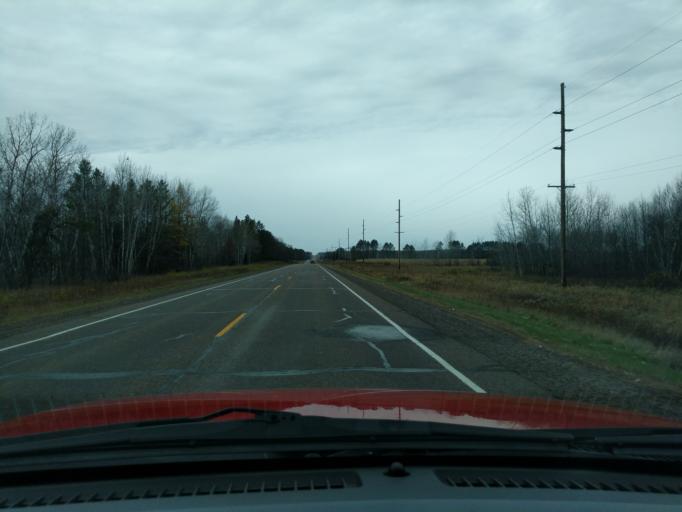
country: US
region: Wisconsin
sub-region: Washburn County
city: Shell Lake
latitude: 45.8151
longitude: -91.9874
